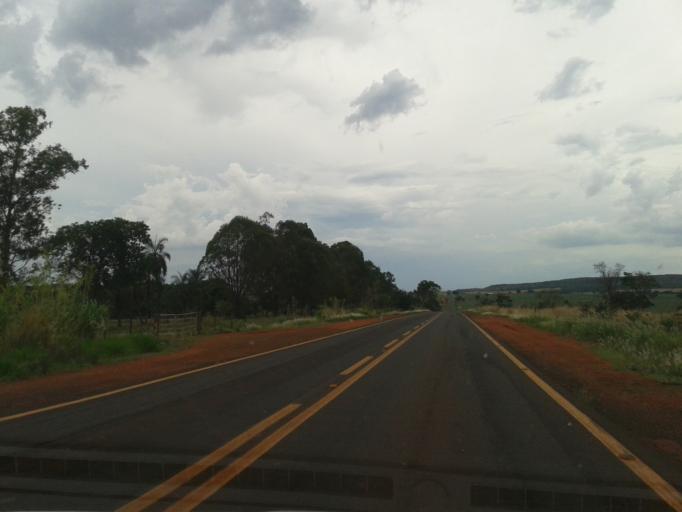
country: BR
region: Minas Gerais
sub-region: Capinopolis
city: Capinopolis
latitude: -18.8071
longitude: -49.5042
